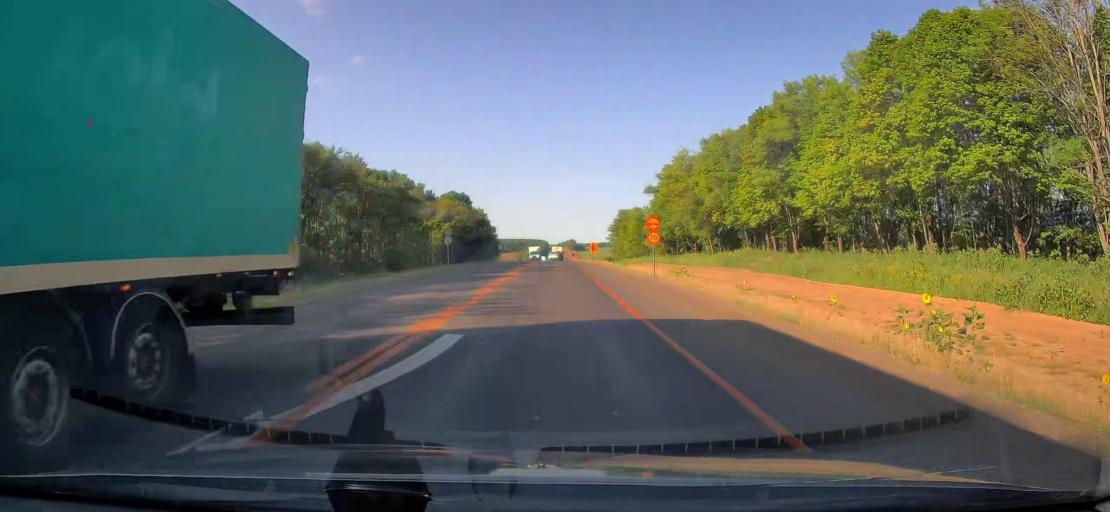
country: RU
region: Tula
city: Bol'shoye Skuratovo
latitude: 53.4187
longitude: 36.7849
